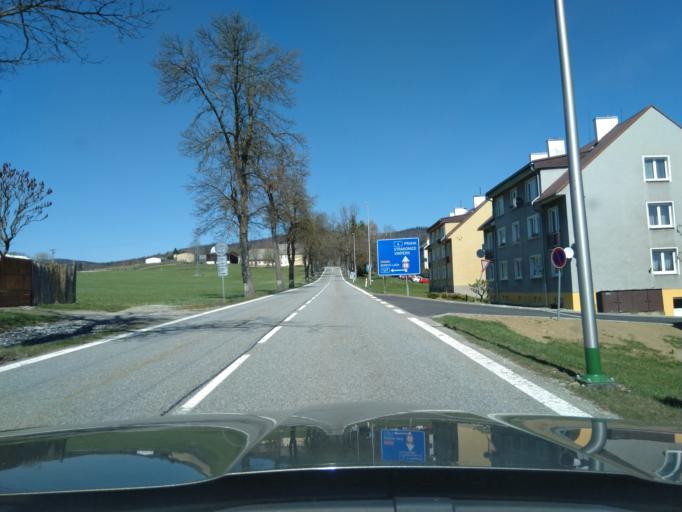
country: CZ
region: Jihocesky
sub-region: Okres Prachatice
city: Borova Lada
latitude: 48.9578
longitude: 13.7582
